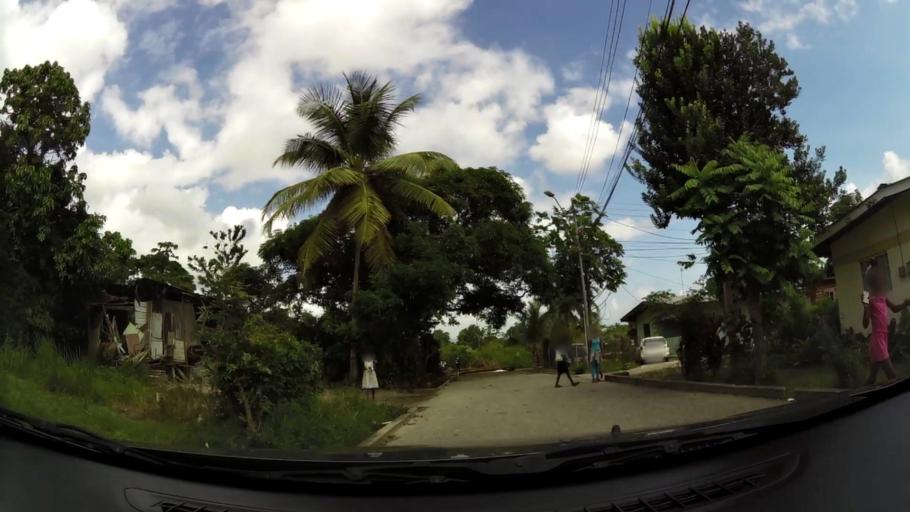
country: TT
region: Borough of Arima
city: Arima
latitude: 10.6326
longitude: -61.2649
